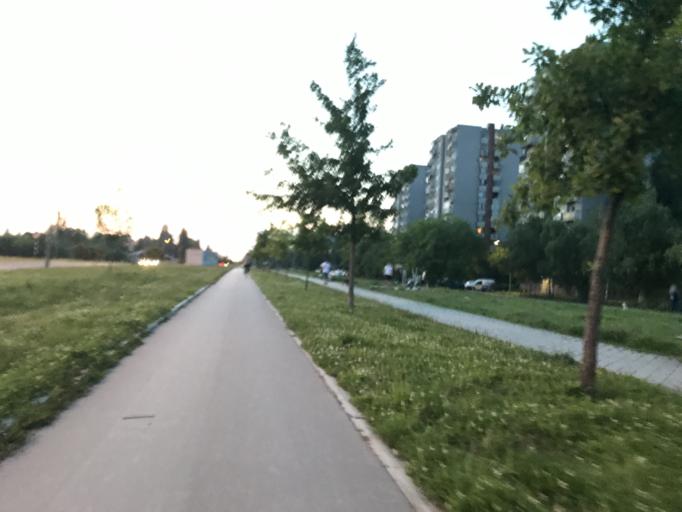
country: RS
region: Autonomna Pokrajina Vojvodina
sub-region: Juznobacki Okrug
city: Novi Sad
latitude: 45.2626
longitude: 19.8073
